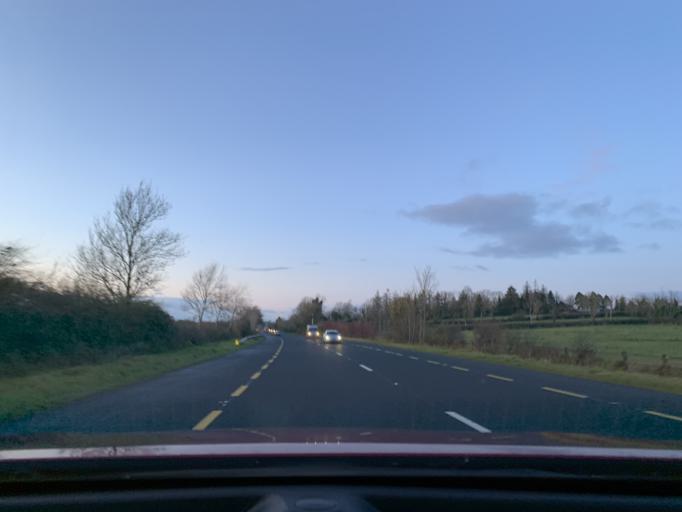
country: IE
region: Connaught
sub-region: County Leitrim
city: Carrick-on-Shannon
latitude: 53.9065
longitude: -7.9614
